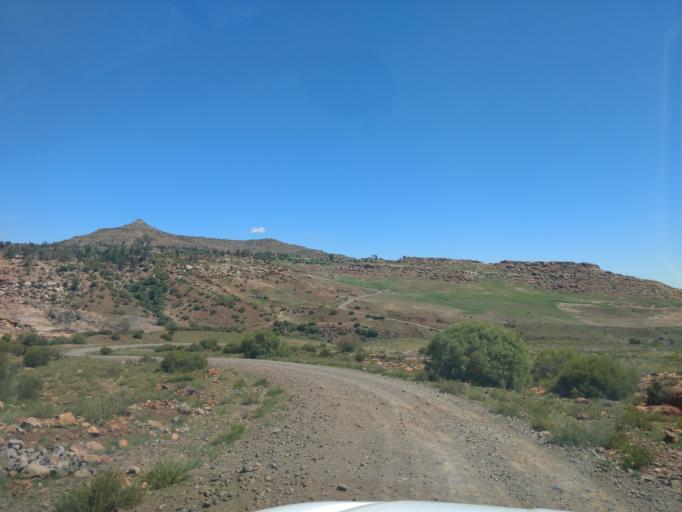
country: LS
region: Maseru
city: Maseru
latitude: -29.4807
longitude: 27.3738
